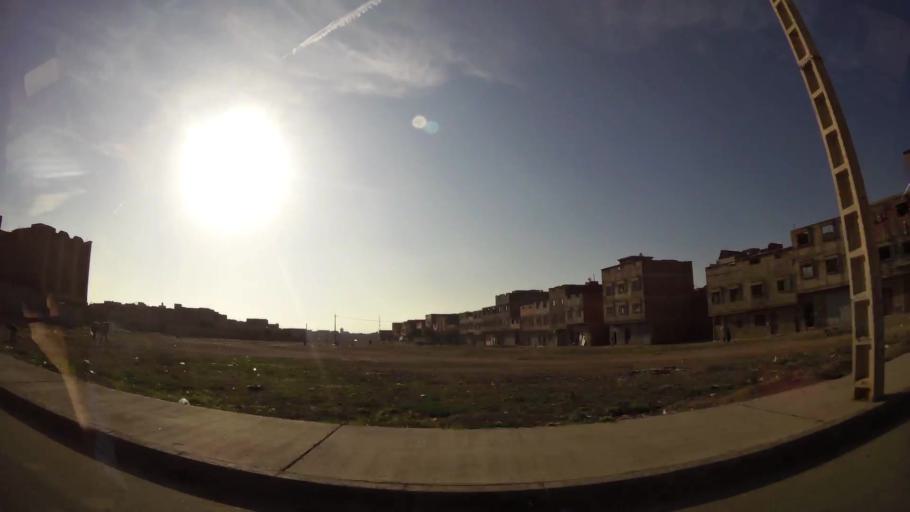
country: MA
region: Oriental
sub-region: Oujda-Angad
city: Oujda
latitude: 34.7122
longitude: -1.8998
